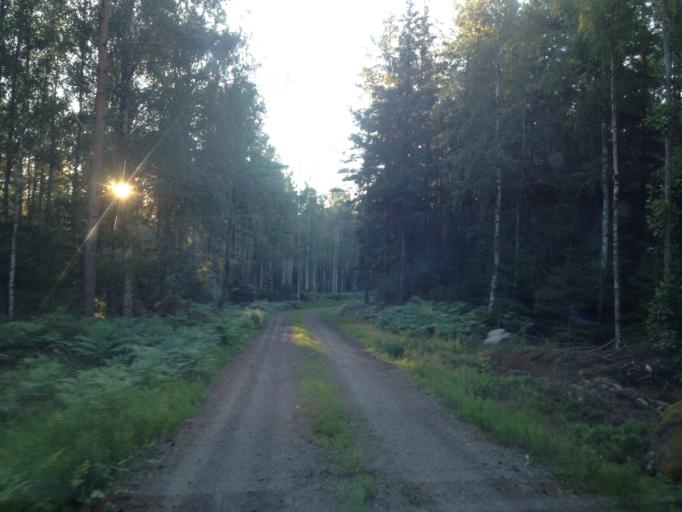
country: SE
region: Kalmar
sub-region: Vasterviks Kommun
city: Overum
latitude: 57.9929
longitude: 16.1707
